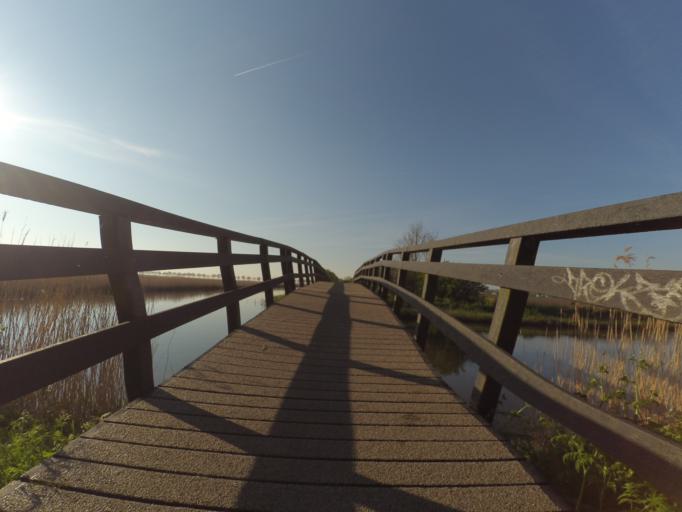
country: NL
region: Flevoland
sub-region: Gemeente Almere
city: Almere Stad
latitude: 52.3929
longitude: 5.3323
